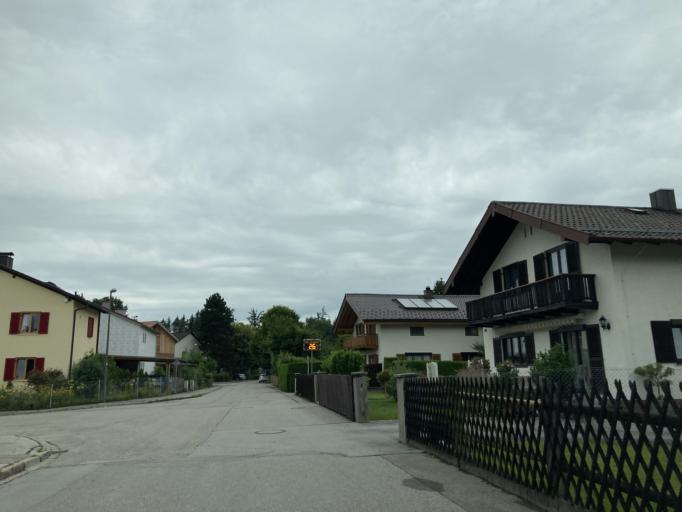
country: DE
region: Bavaria
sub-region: Upper Bavaria
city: Stephanskirchen
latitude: 47.8631
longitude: 12.1777
